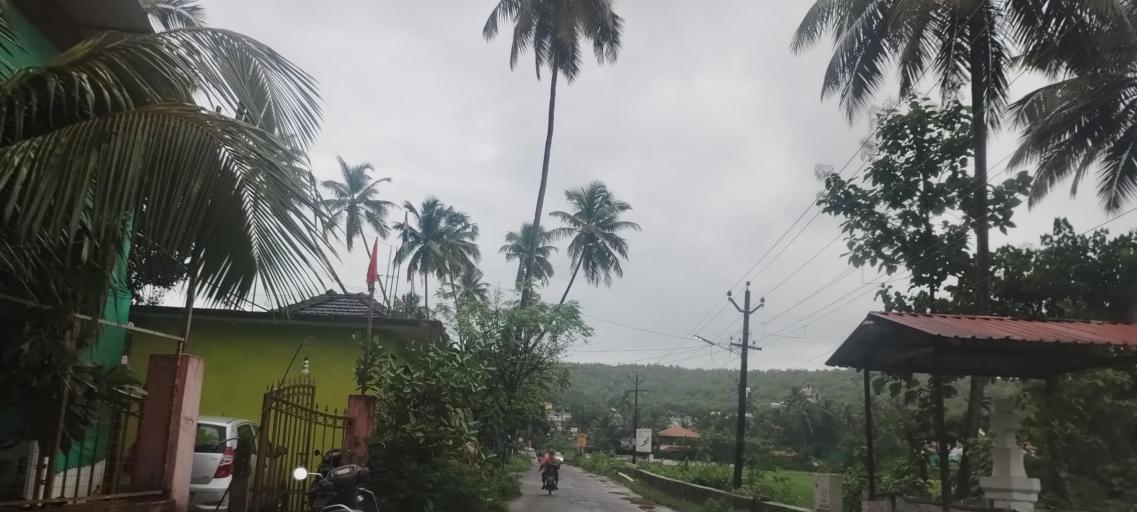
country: IN
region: Goa
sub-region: North Goa
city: Solim
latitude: 15.5952
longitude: 73.7724
